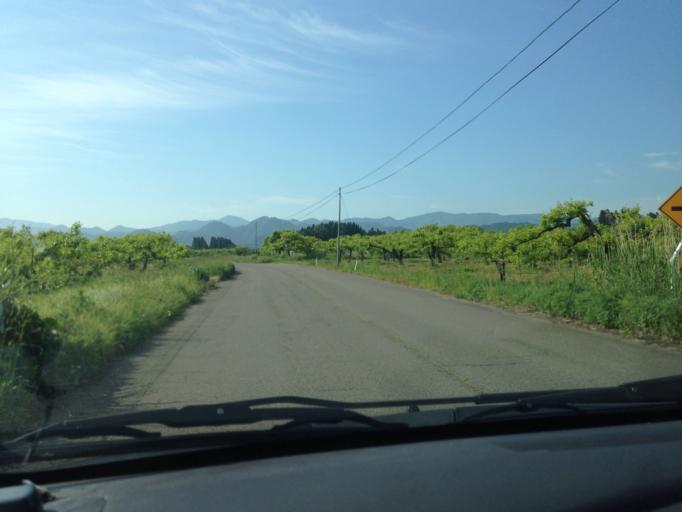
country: JP
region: Fukushima
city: Kitakata
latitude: 37.4552
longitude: 139.8184
